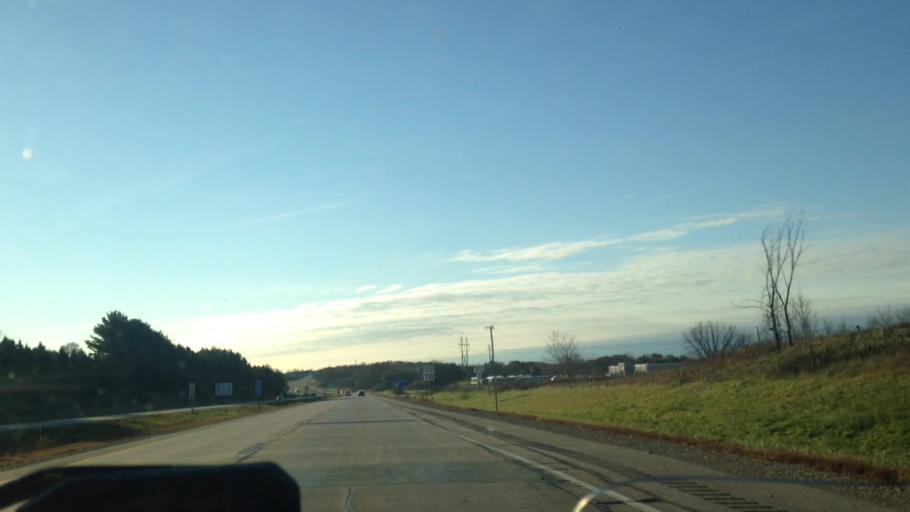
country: US
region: Wisconsin
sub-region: Washington County
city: Slinger
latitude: 43.3620
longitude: -88.2932
